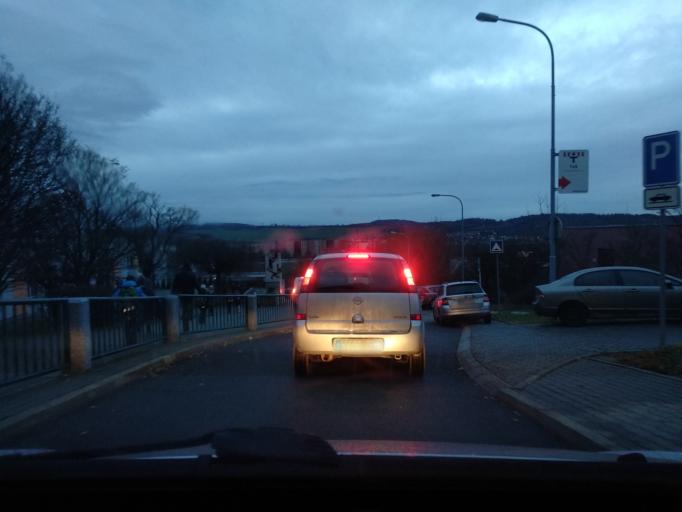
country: CZ
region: South Moravian
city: Ostopovice
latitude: 49.1751
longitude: 16.5526
